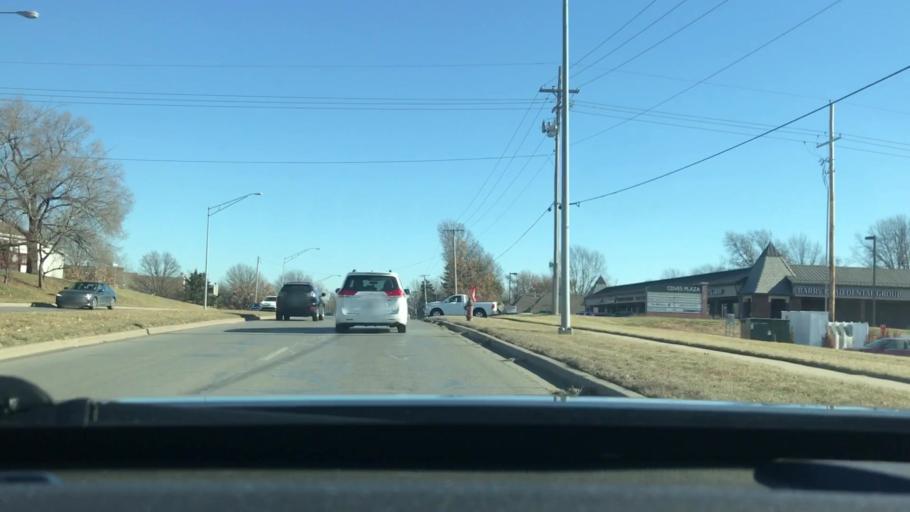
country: US
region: Missouri
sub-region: Platte County
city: Weatherby Lake
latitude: 39.2467
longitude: -94.6454
